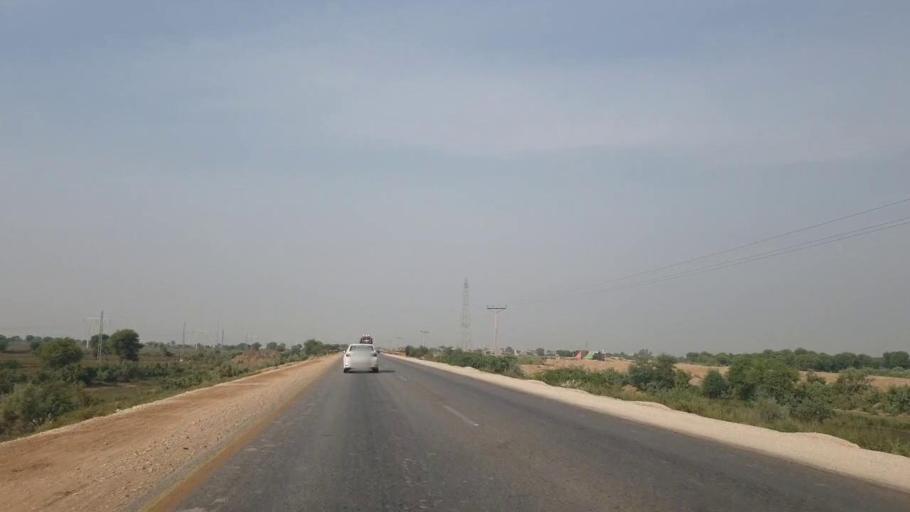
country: PK
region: Sindh
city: Sann
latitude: 26.0810
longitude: 68.0944
